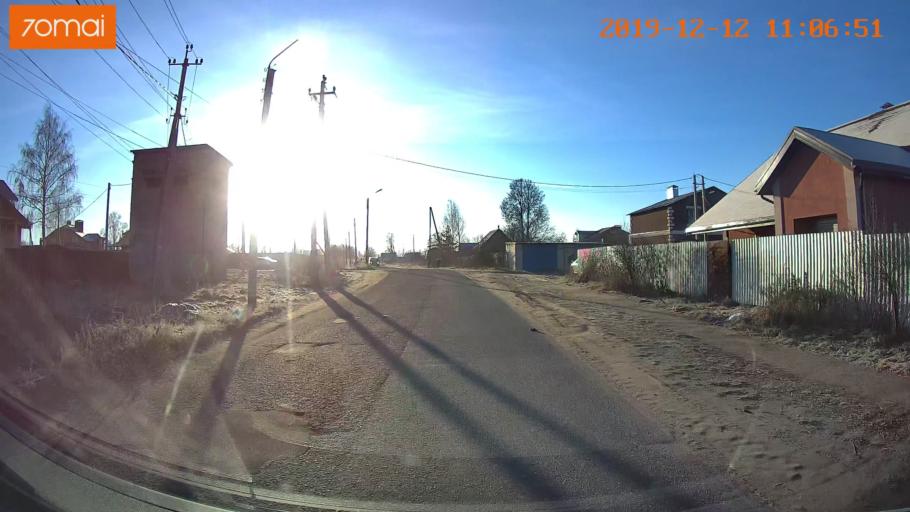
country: RU
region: Ivanovo
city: Kokhma
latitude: 56.9410
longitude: 41.0884
